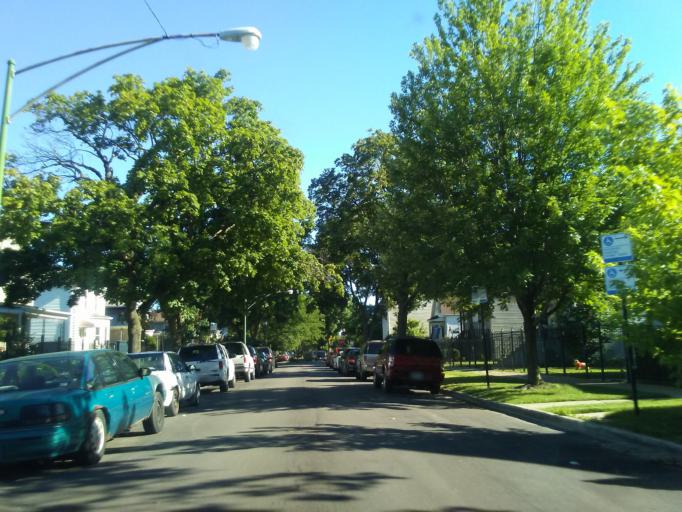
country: US
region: Illinois
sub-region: Cook County
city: Oak Park
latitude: 41.9196
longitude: -87.7377
